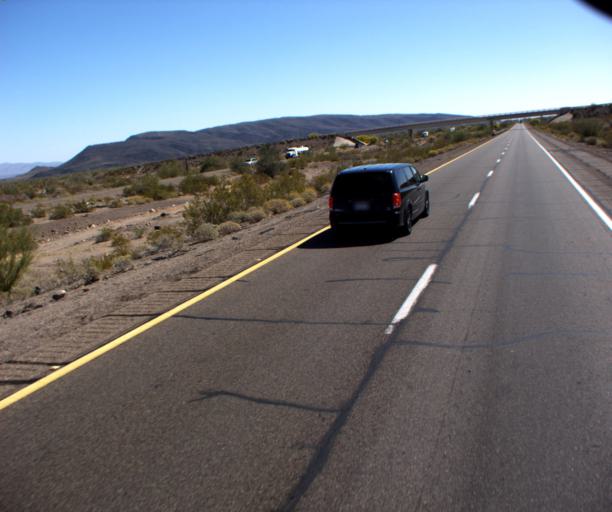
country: US
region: Arizona
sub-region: La Paz County
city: Quartzsite
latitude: 33.6564
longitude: -113.9687
